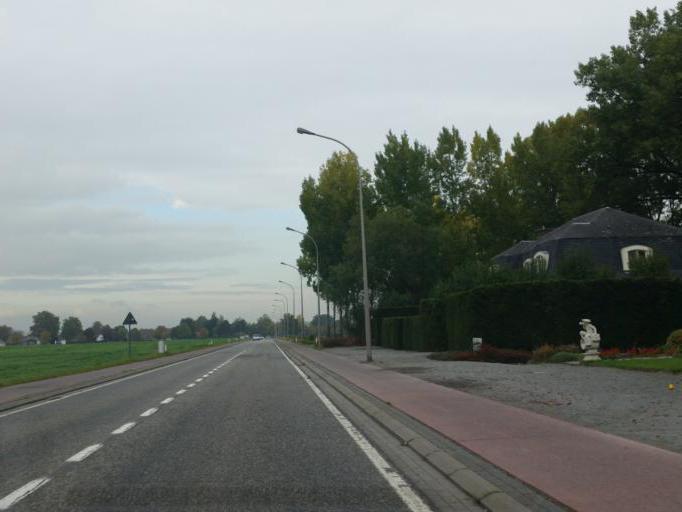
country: BE
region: Flanders
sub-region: Provincie Vlaams-Brabant
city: Steenokkerzeel
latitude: 50.9219
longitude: 4.4993
